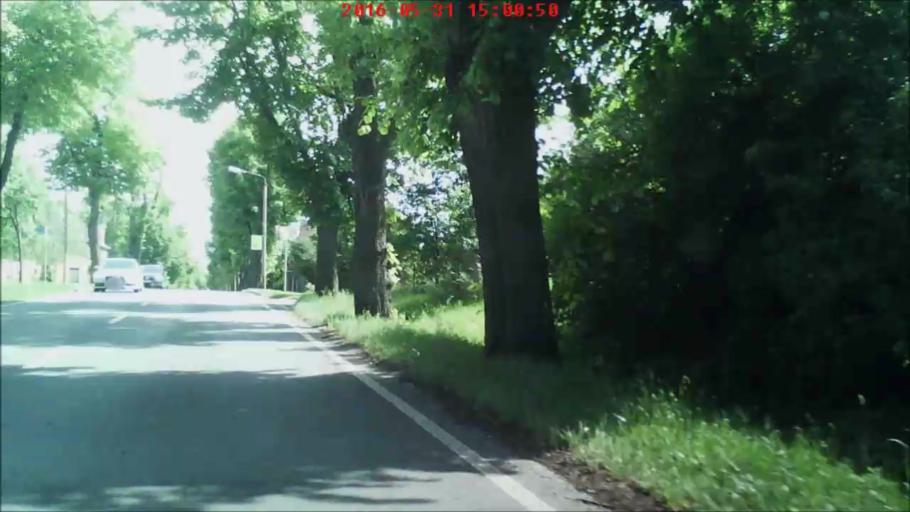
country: DE
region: Thuringia
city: Straussfurt
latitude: 51.1678
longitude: 10.9884
